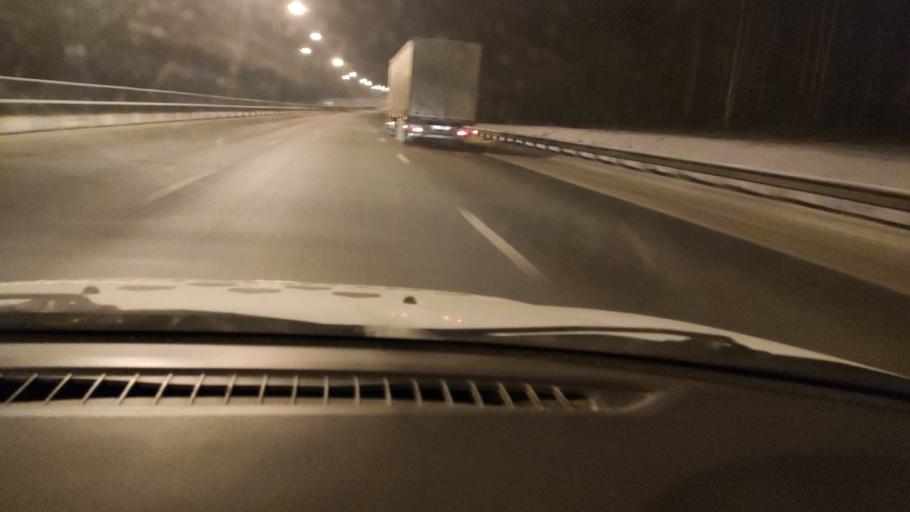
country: RU
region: Perm
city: Zvezdnyy
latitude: 57.7451
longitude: 56.3358
